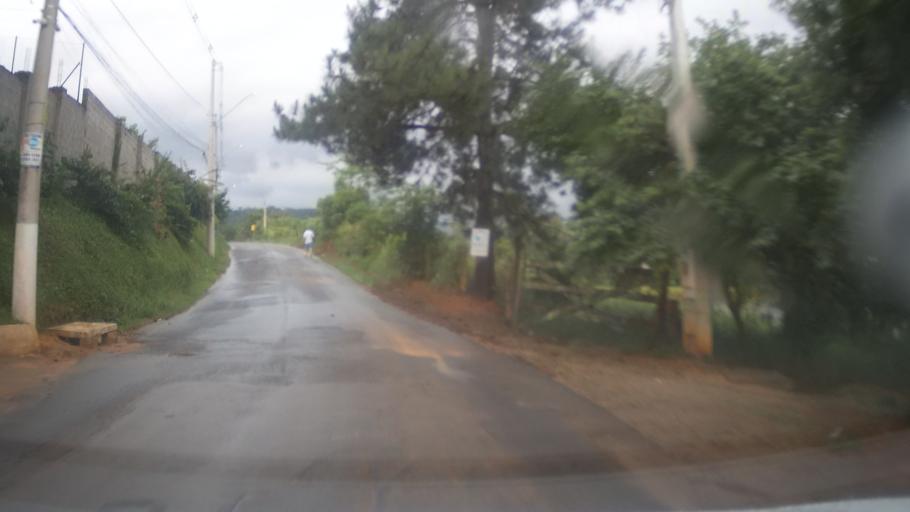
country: BR
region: Sao Paulo
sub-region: Itupeva
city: Itupeva
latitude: -23.1628
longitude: -47.0645
